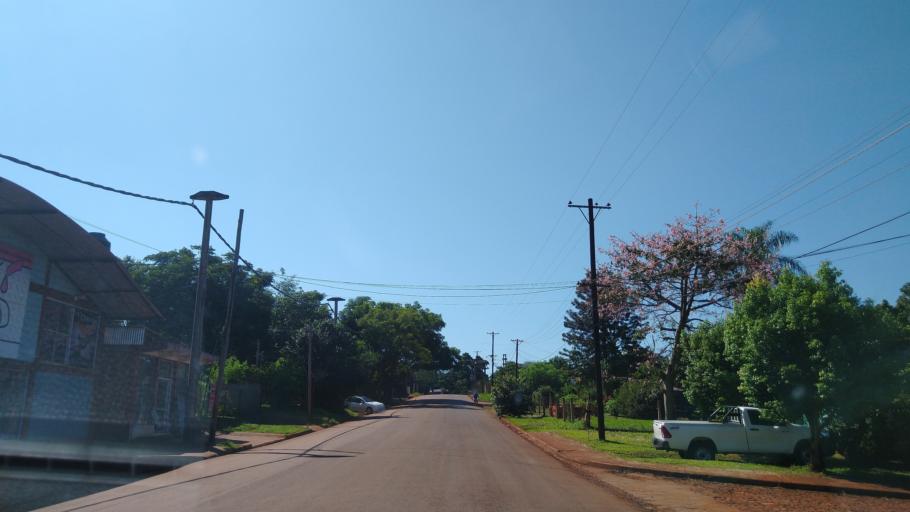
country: AR
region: Misiones
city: Puerto Libertad
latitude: -25.9771
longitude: -54.5738
